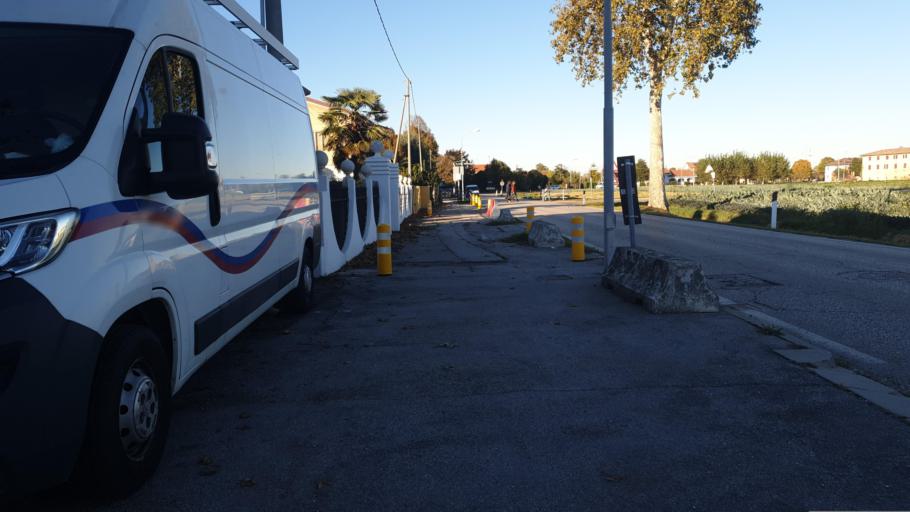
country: IT
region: Veneto
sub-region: Provincia di Venezia
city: Ballo
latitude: 45.4571
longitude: 12.0726
